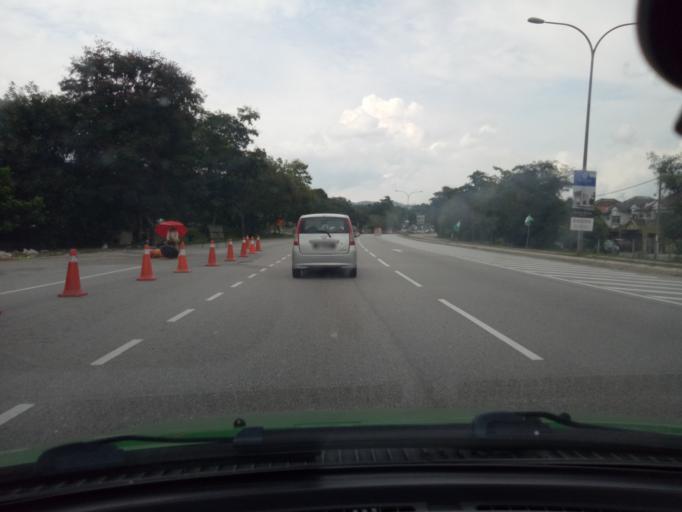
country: MY
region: Selangor
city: Kampong Baharu Balakong
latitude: 3.0105
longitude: 101.7899
